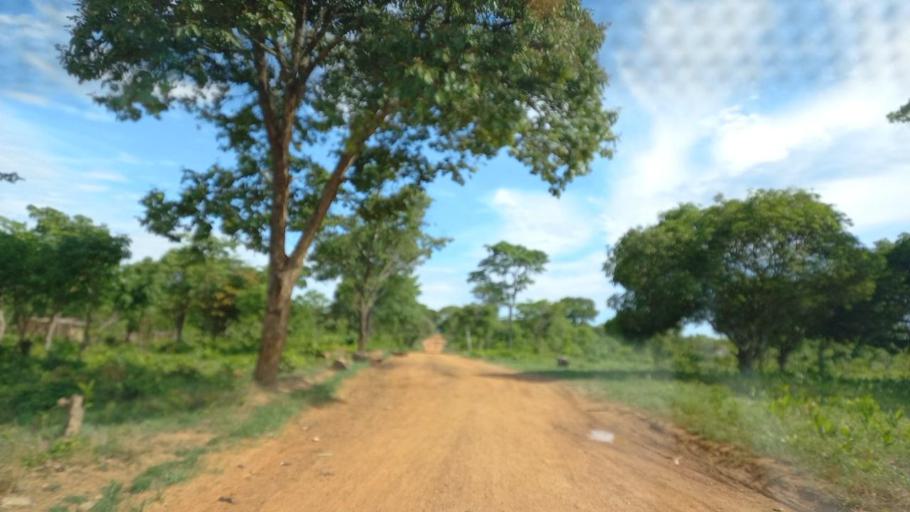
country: ZM
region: North-Western
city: Kabompo
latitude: -13.0715
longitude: 24.2181
